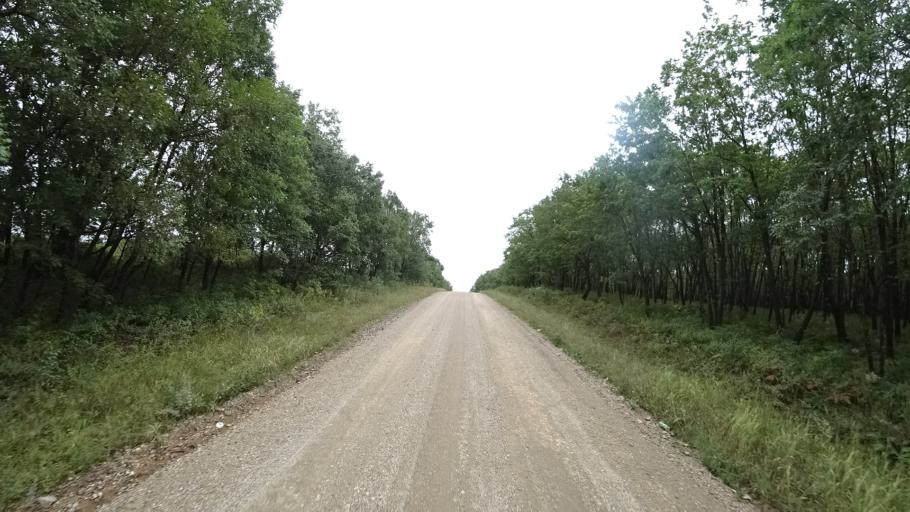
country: RU
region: Primorskiy
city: Ivanovka
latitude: 44.0360
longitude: 132.5008
